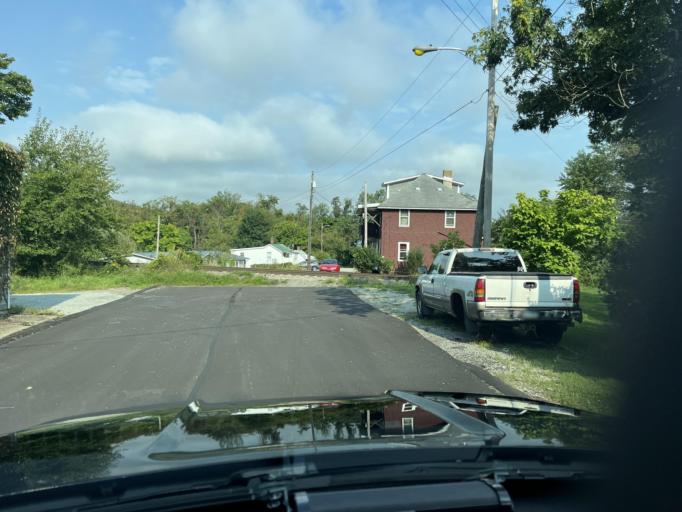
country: US
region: Pennsylvania
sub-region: Fayette County
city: Hopwood
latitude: 39.8605
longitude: -79.7139
